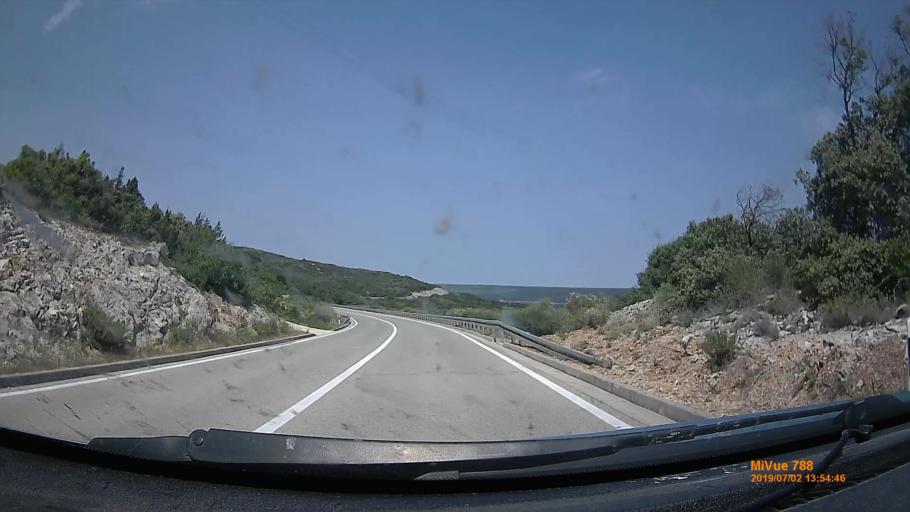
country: HR
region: Primorsko-Goranska
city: Mali Losinj
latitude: 44.6424
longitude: 14.3912
